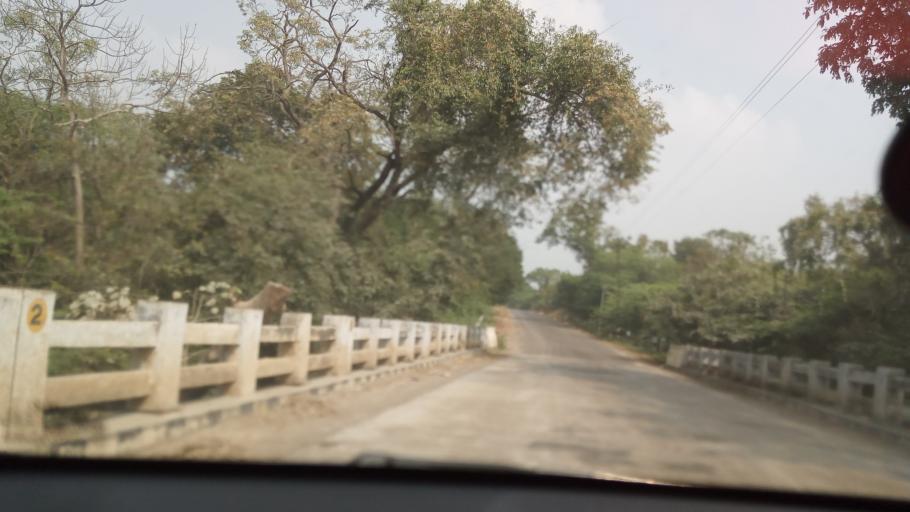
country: IN
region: Tamil Nadu
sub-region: Erode
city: Sathyamangalam
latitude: 11.5447
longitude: 77.1394
